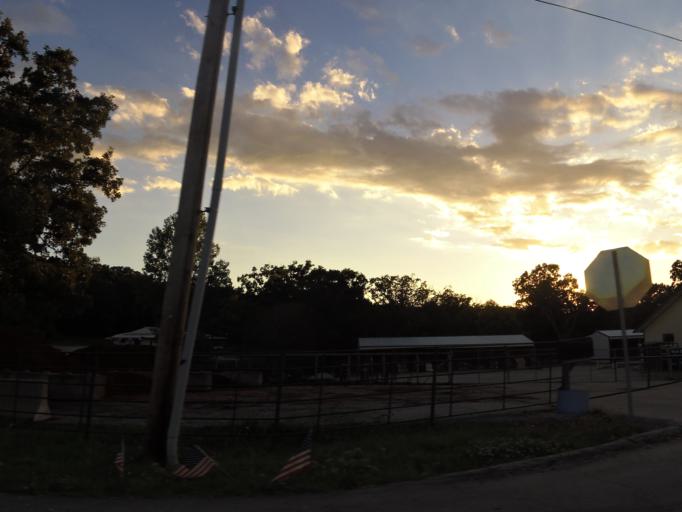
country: US
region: Missouri
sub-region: Jefferson County
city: Cedar Hill
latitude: 38.3358
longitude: -90.6474
